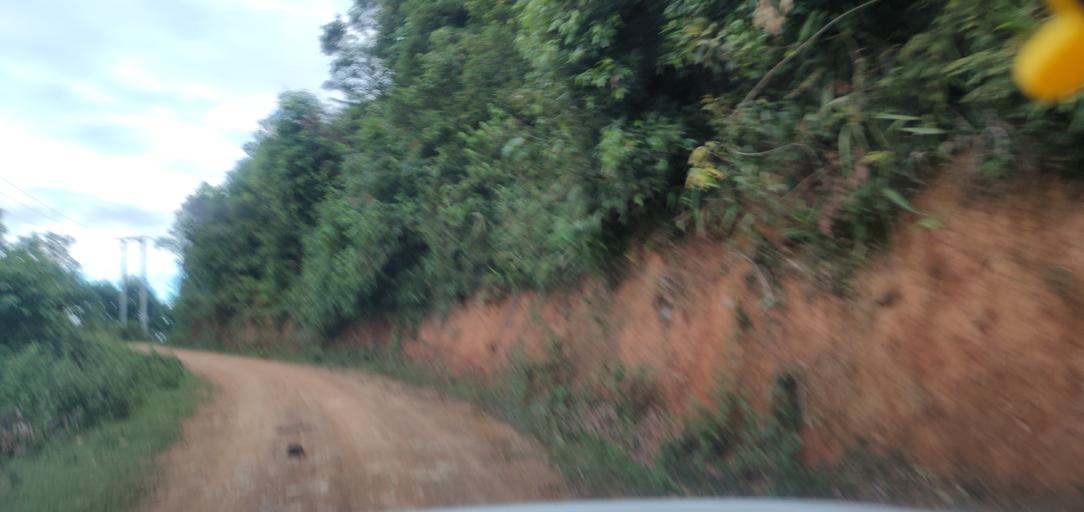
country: LA
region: Phongsali
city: Khoa
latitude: 21.1959
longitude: 102.2586
